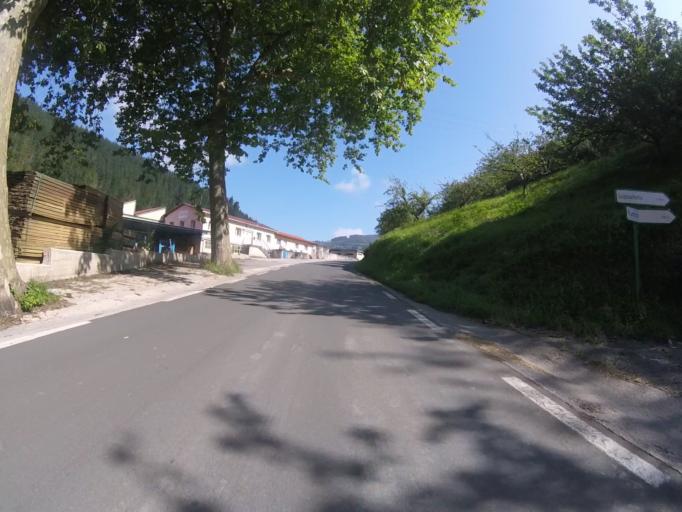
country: ES
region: Basque Country
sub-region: Provincia de Guipuzcoa
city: Ormaiztegui
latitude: 43.0645
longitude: -2.2383
